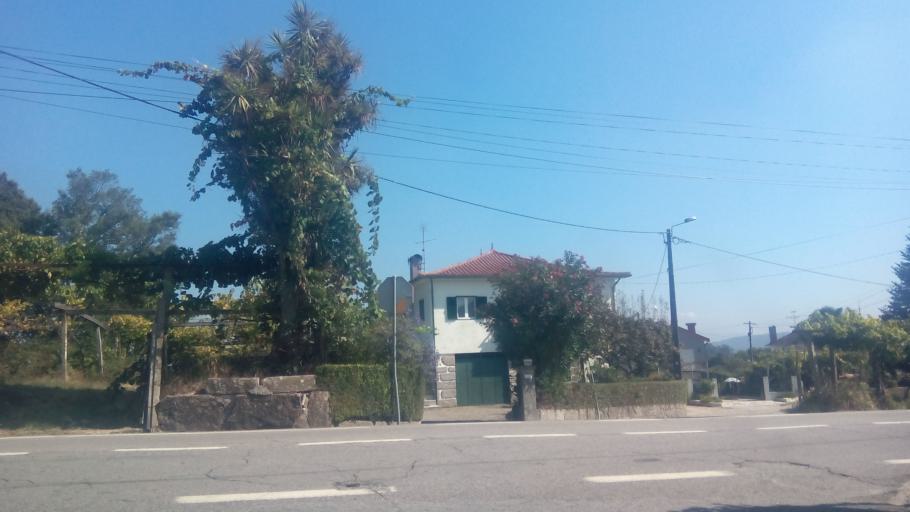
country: PT
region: Porto
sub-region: Paredes
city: Baltar
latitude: 41.1888
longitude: -8.3891
